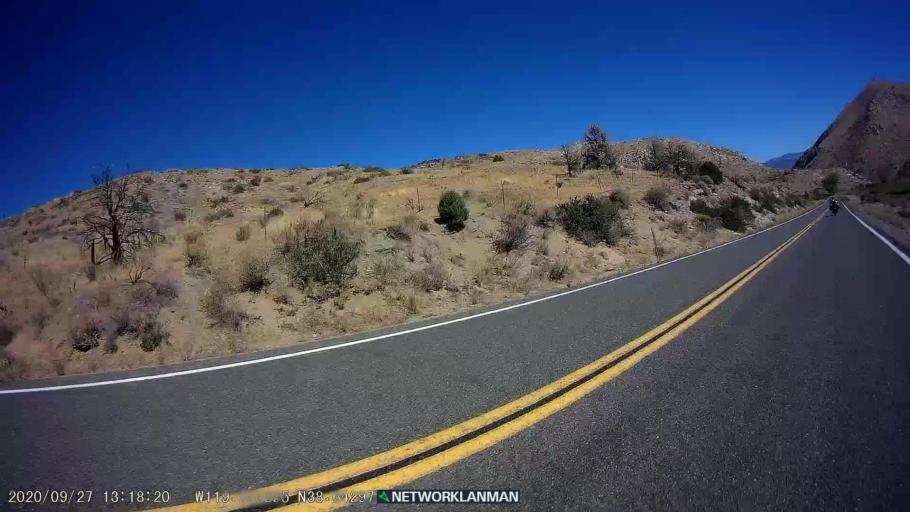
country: US
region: Nevada
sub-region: Lyon County
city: Smith Valley
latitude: 38.6431
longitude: -119.5548
